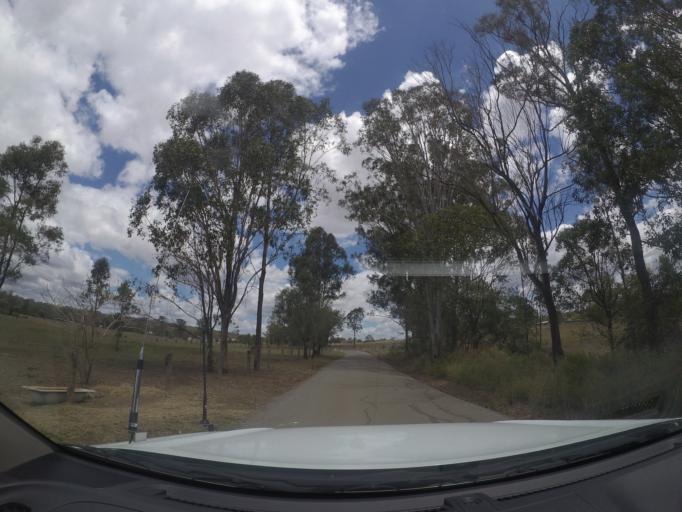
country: AU
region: Queensland
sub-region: Logan
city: Cedar Vale
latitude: -27.9397
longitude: 153.0663
